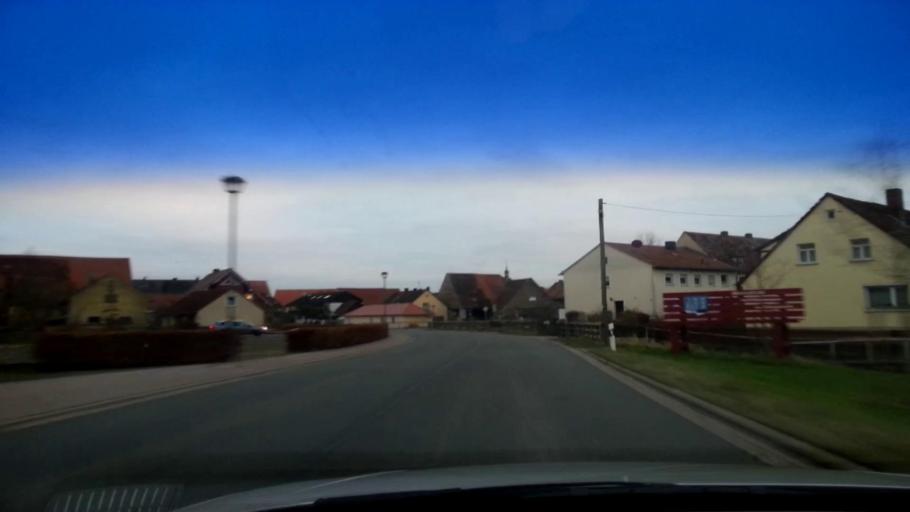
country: DE
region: Bavaria
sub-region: Upper Franconia
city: Pommersfelden
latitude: 49.7745
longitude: 10.8023
